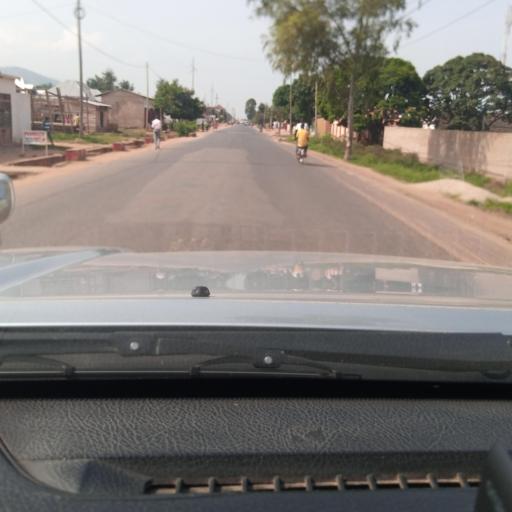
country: BI
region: Bujumbura Mairie
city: Bujumbura
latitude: -3.4589
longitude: 29.3509
